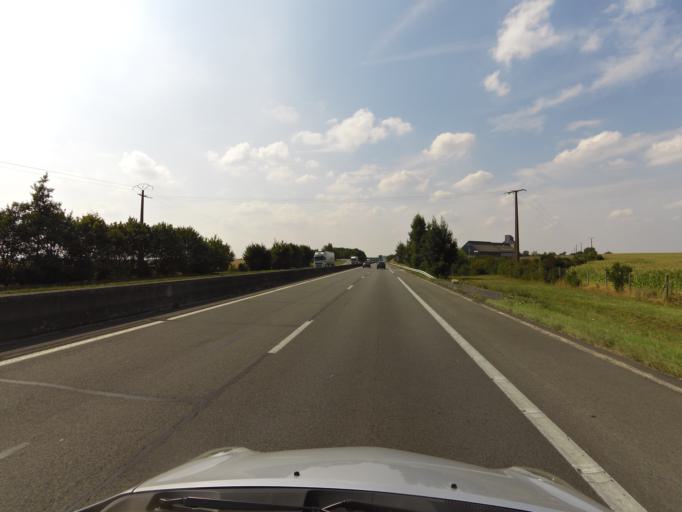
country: FR
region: Picardie
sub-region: Departement de l'Aisne
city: Couvron-et-Aumencourt
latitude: 49.6870
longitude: 3.4763
